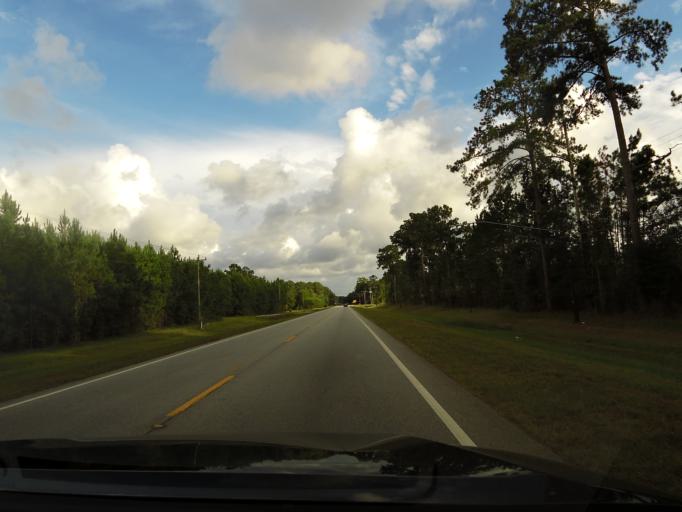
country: US
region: Georgia
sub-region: Liberty County
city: Midway
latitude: 31.7304
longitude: -81.4278
